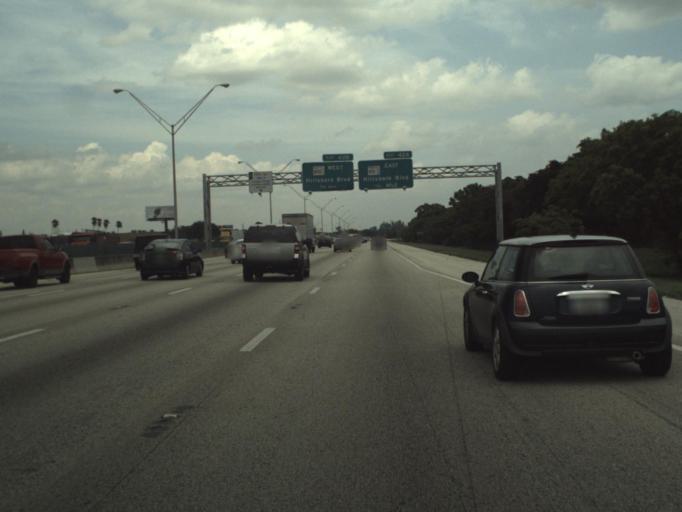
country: US
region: Florida
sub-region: Broward County
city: Deerfield Beach
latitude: 26.3075
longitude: -80.1186
